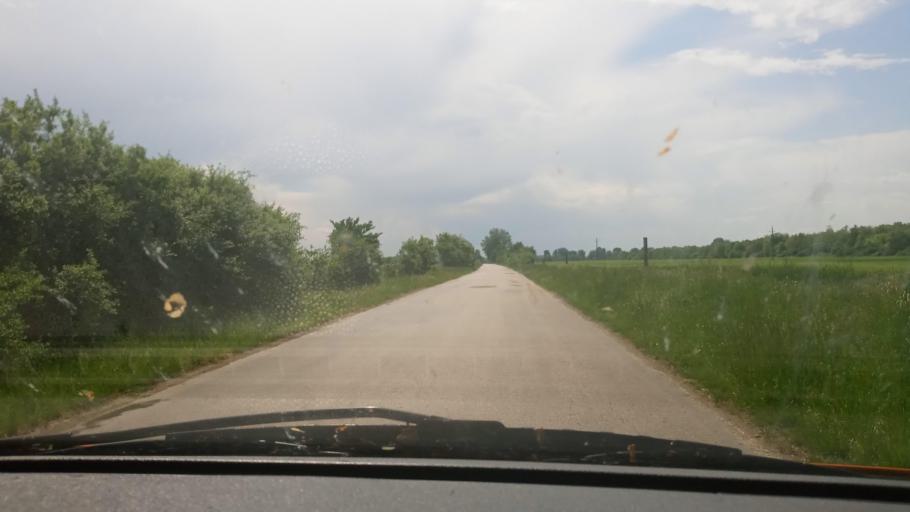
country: HU
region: Baranya
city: Siklos
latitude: 45.8193
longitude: 18.3558
